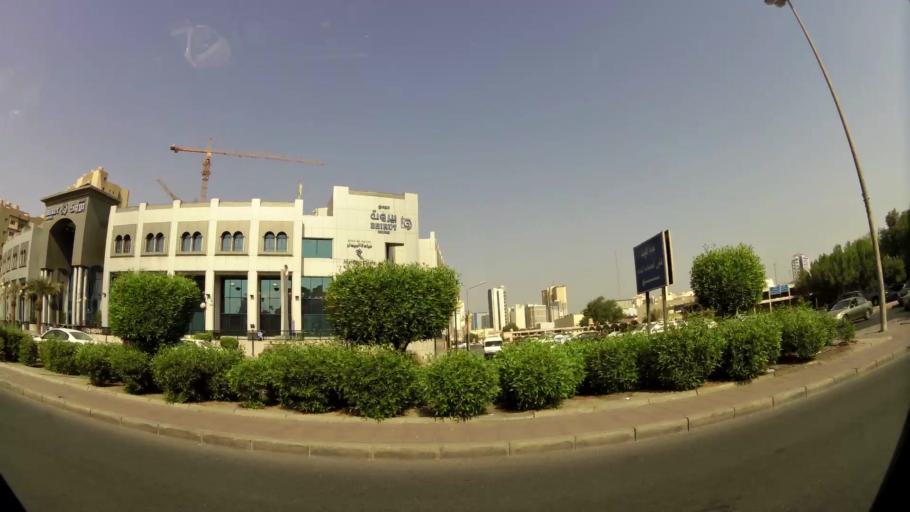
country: KW
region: Muhafazat Hawalli
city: Hawalli
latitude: 29.3367
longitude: 48.0215
